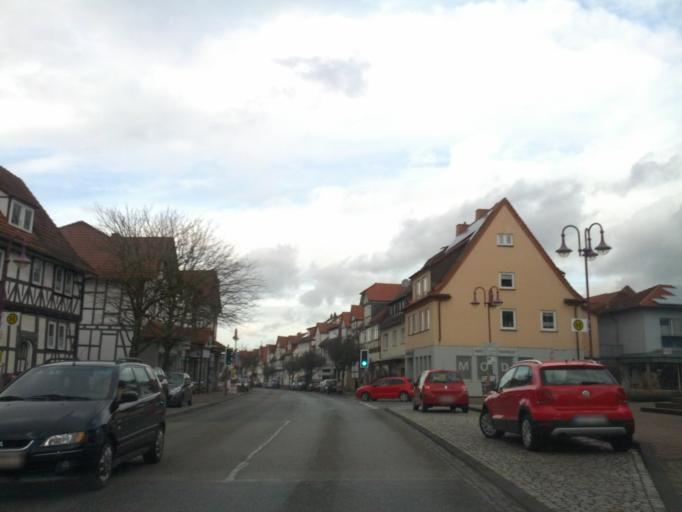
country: DE
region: Hesse
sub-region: Regierungsbezirk Kassel
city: Kaufungen
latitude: 51.2826
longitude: 9.6341
